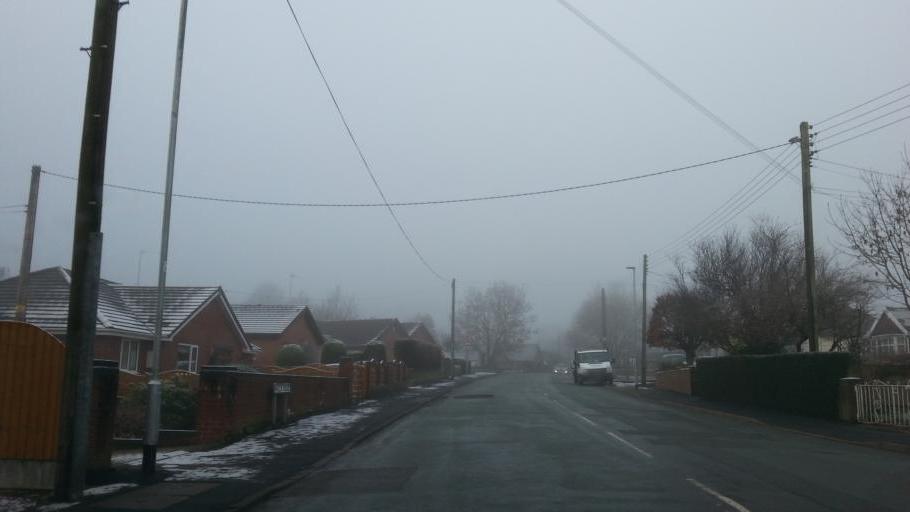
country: GB
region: England
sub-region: Staffordshire
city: Biddulph
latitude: 53.1220
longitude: -2.1771
